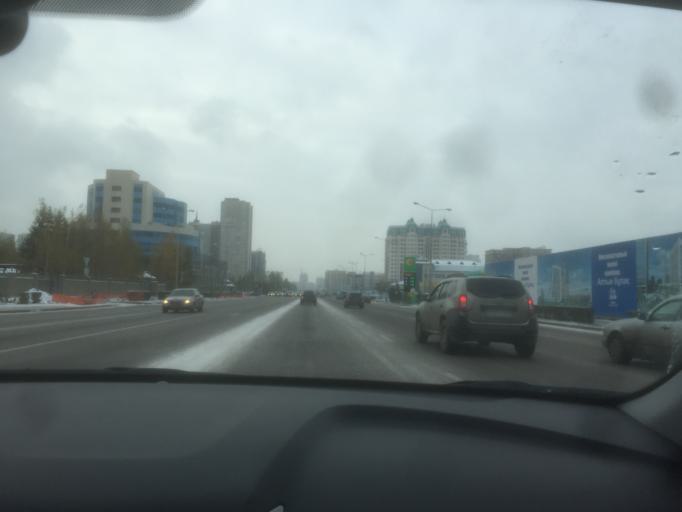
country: KZ
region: Astana Qalasy
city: Astana
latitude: 51.1432
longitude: 71.4620
